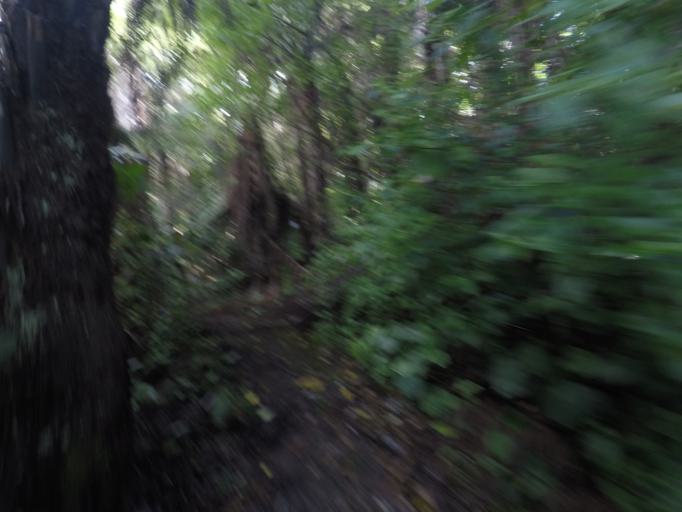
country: NZ
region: Auckland
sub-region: Auckland
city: Rosebank
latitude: -36.8792
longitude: 174.6667
